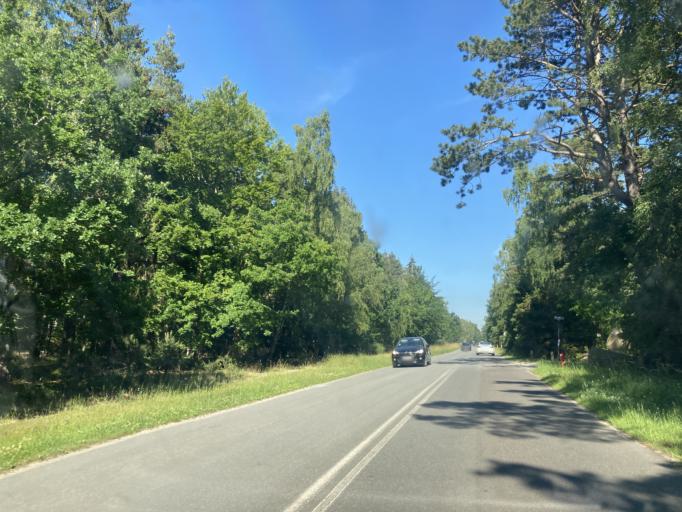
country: DK
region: Capital Region
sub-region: Halsnaes Kommune
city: Frederiksvaerk
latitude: 56.0115
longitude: 12.0147
